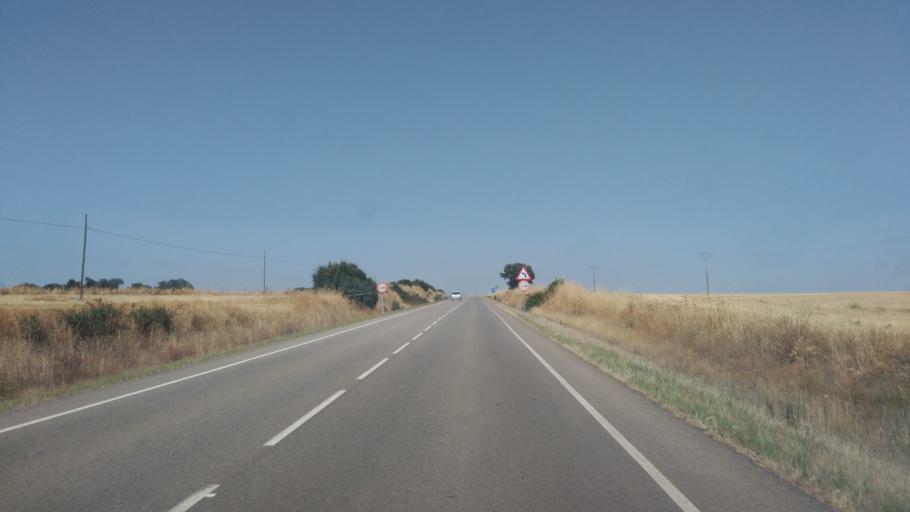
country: ES
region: Castille and Leon
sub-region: Provincia de Salamanca
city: Cabrillas
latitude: 40.7523
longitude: -6.1861
